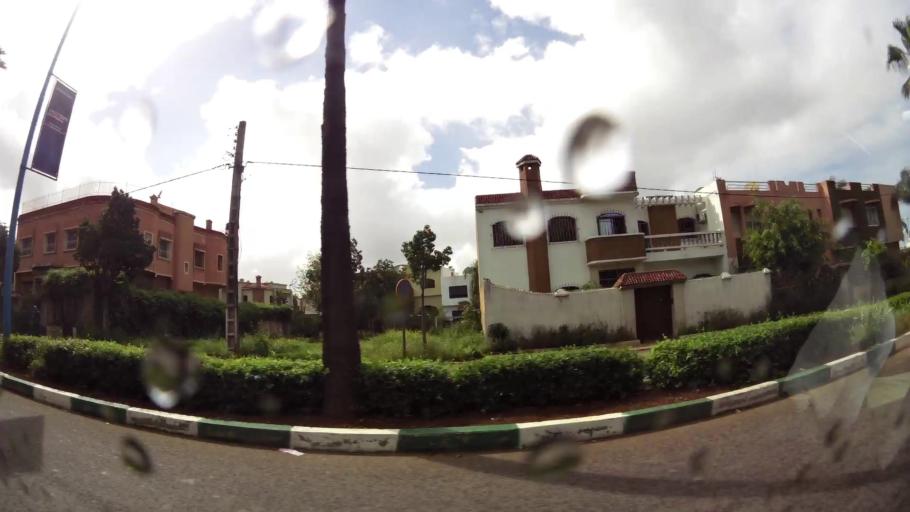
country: MA
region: Grand Casablanca
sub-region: Casablanca
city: Casablanca
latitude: 33.5360
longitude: -7.6451
